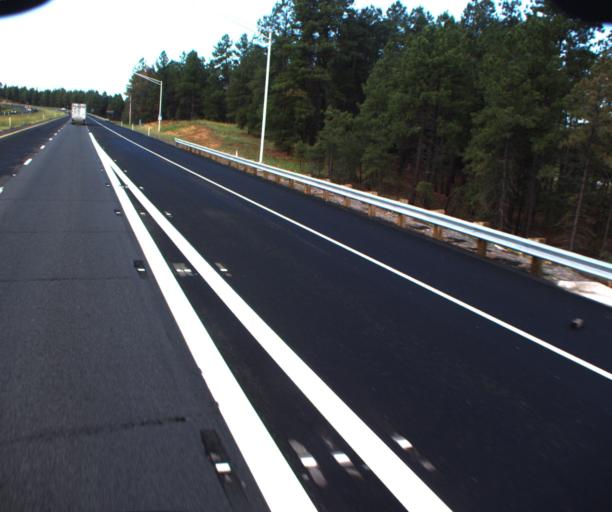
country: US
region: Arizona
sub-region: Coconino County
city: Kachina Village
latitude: 35.1351
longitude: -111.6850
